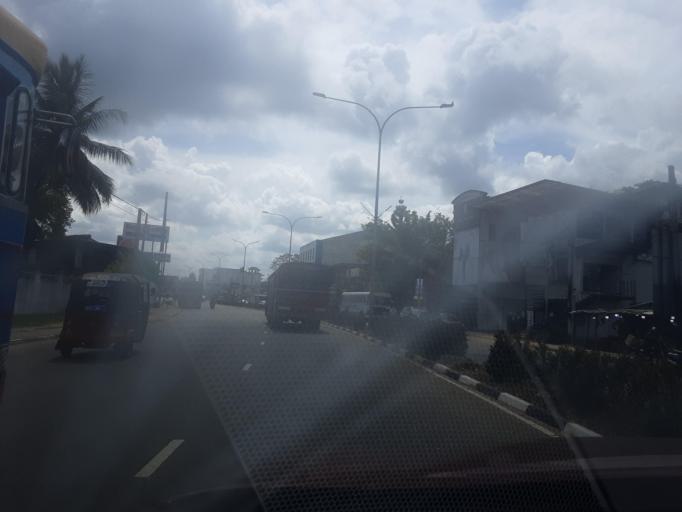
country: LK
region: North Western
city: Kuliyapitiya
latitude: 7.4691
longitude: 80.0327
